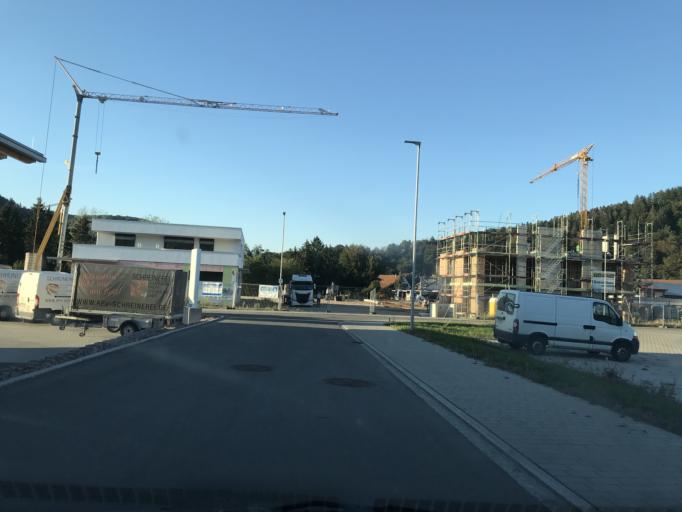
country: DE
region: Baden-Wuerttemberg
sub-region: Freiburg Region
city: Maulburg
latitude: 47.6463
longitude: 7.7997
